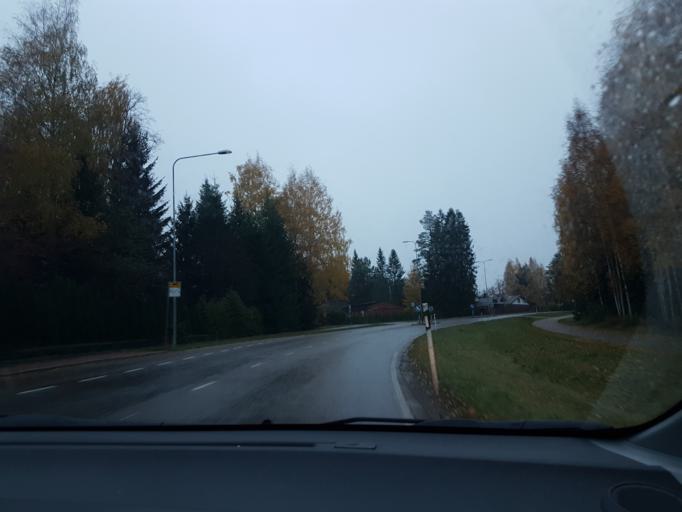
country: FI
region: Uusimaa
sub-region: Helsinki
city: Tuusula
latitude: 60.3979
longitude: 24.9821
